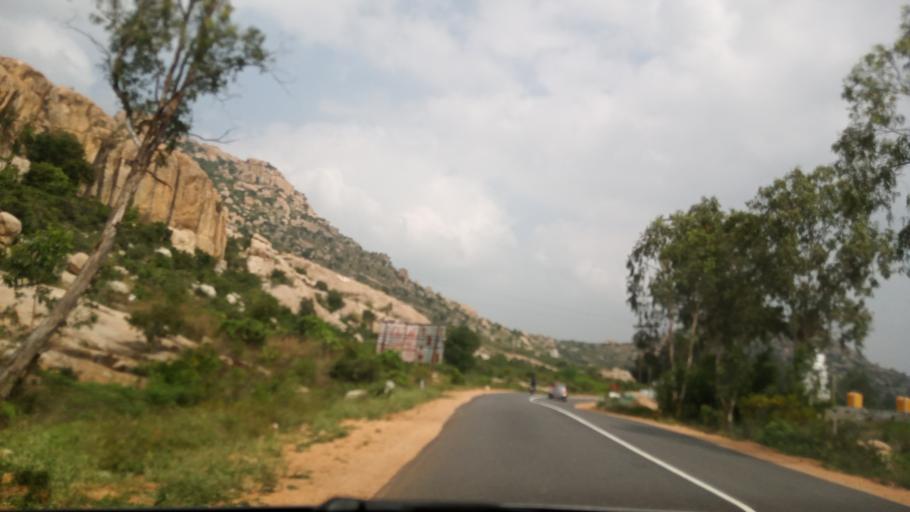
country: IN
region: Andhra Pradesh
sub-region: Chittoor
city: Madanapalle
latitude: 13.6352
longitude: 78.6081
